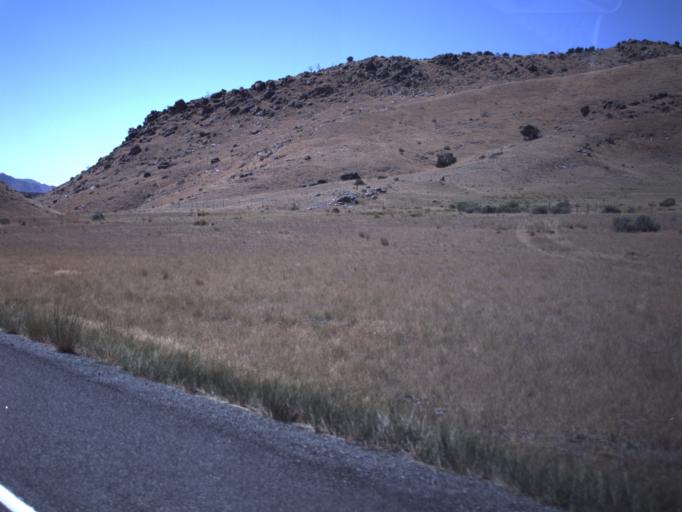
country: US
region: Utah
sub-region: Juab County
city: Nephi
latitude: 39.6464
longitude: -112.0811
